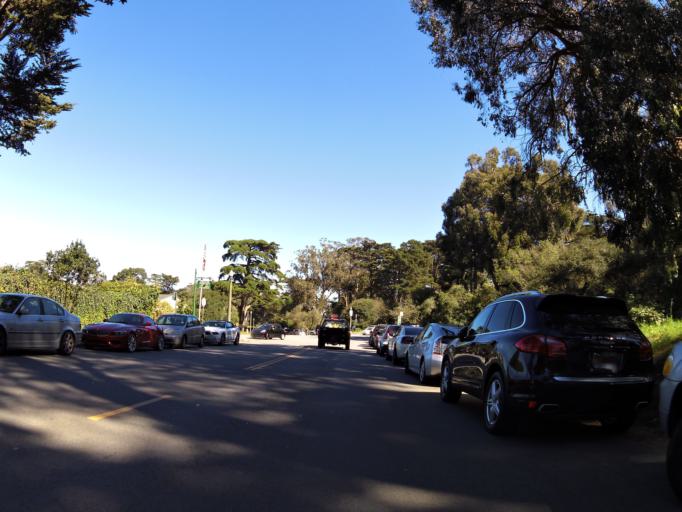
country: US
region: California
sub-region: San Francisco County
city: San Francisco
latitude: 37.7671
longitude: -122.4614
